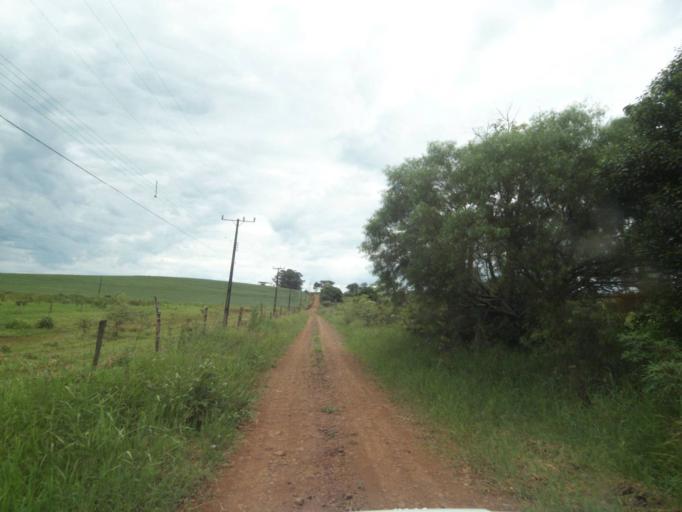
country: BR
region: Parana
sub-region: Guaraniacu
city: Guaraniacu
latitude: -24.9251
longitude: -52.9372
